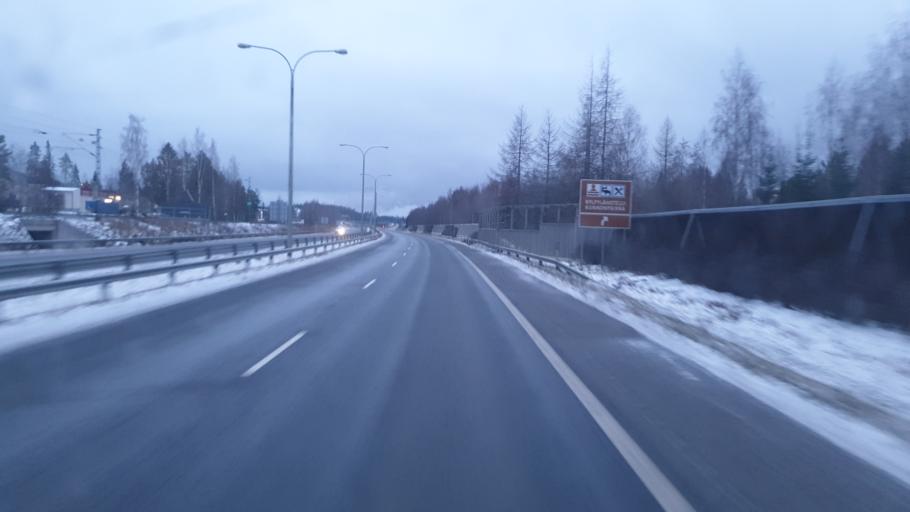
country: FI
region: Northern Savo
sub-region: Kuopio
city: Kuopio
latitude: 62.9812
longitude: 27.7060
